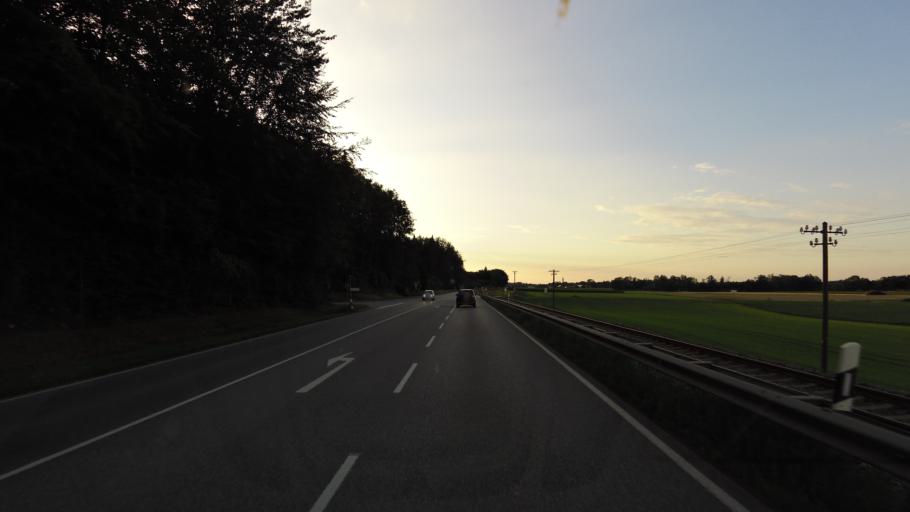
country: DE
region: Bavaria
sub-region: Upper Bavaria
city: Nussdorf
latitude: 47.9174
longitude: 12.6061
